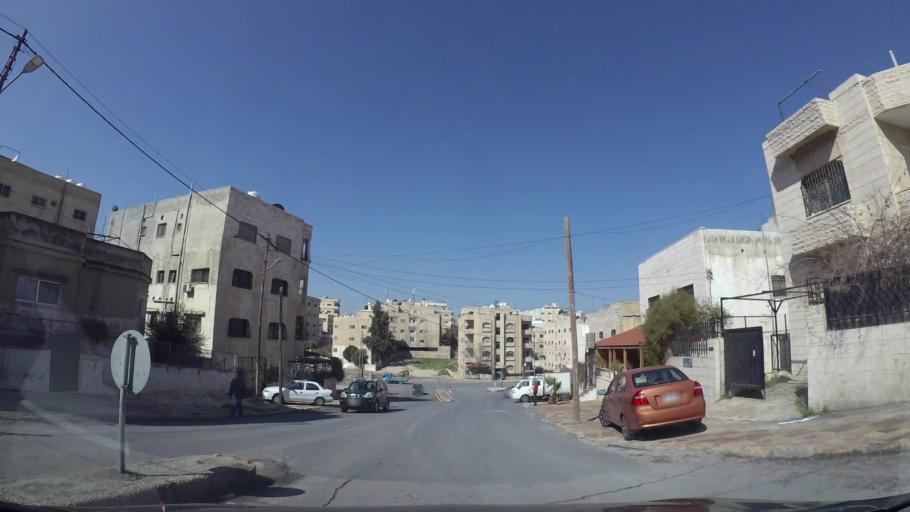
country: JO
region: Amman
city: Amman
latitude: 31.9863
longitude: 35.9843
